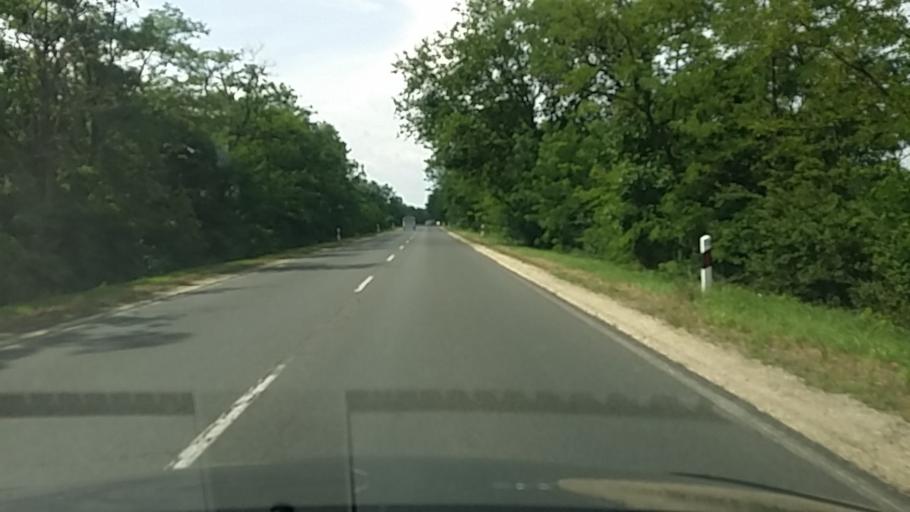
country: HU
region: Pest
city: Taborfalva
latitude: 47.1016
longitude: 19.4679
